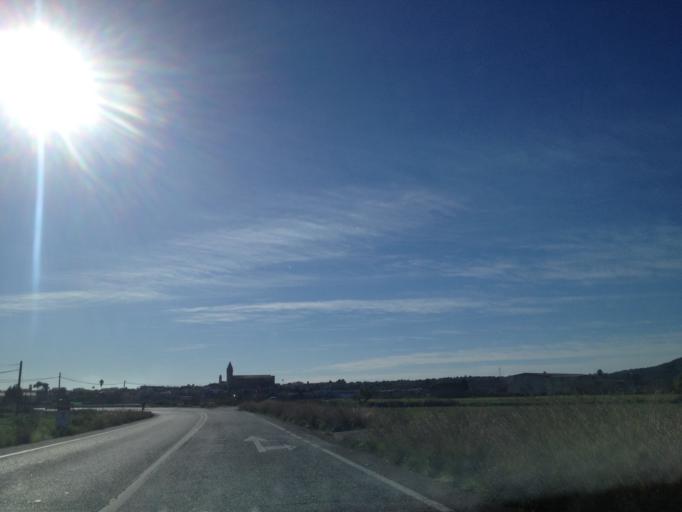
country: ES
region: Balearic Islands
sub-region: Illes Balears
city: Petra
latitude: 39.6229
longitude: 3.1100
